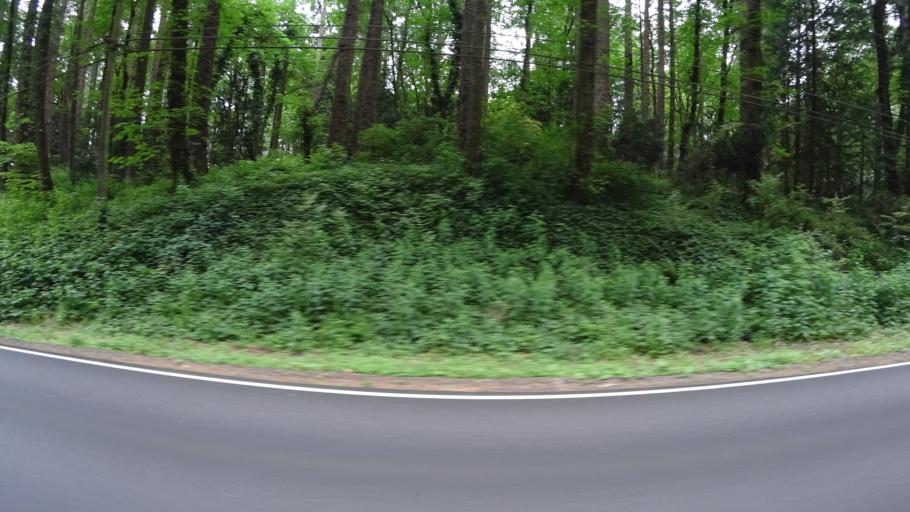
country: US
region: Oregon
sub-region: Clackamas County
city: Lake Oswego
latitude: 45.4272
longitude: -122.6628
